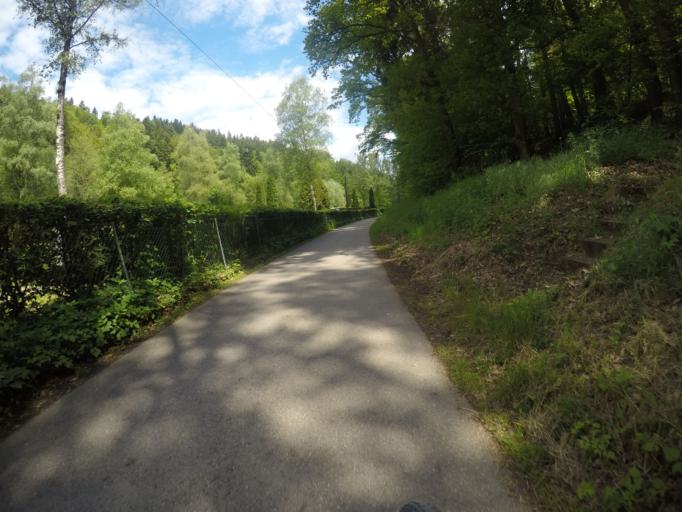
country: DE
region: Baden-Wuerttemberg
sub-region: Karlsruhe Region
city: Wildberg
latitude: 48.6127
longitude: 8.7358
